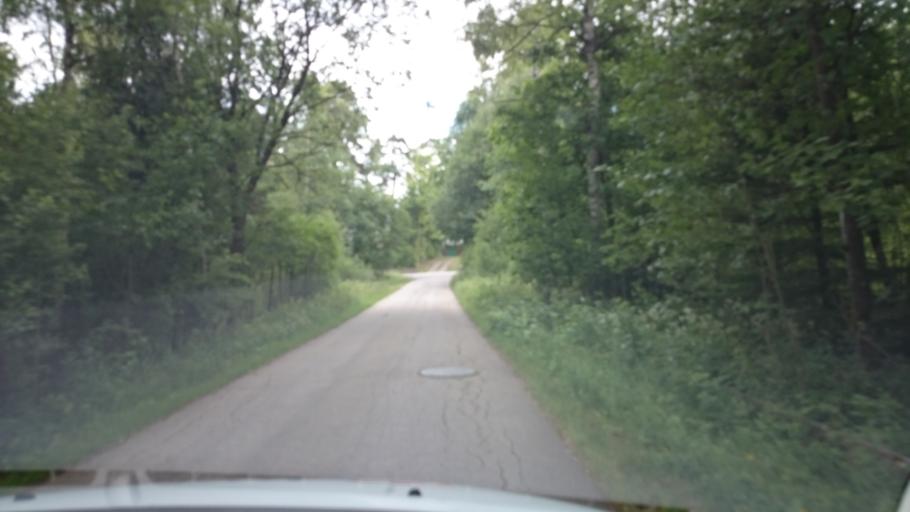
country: SE
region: Halland
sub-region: Hylte Kommun
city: Torup
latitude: 56.9614
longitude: 13.1508
